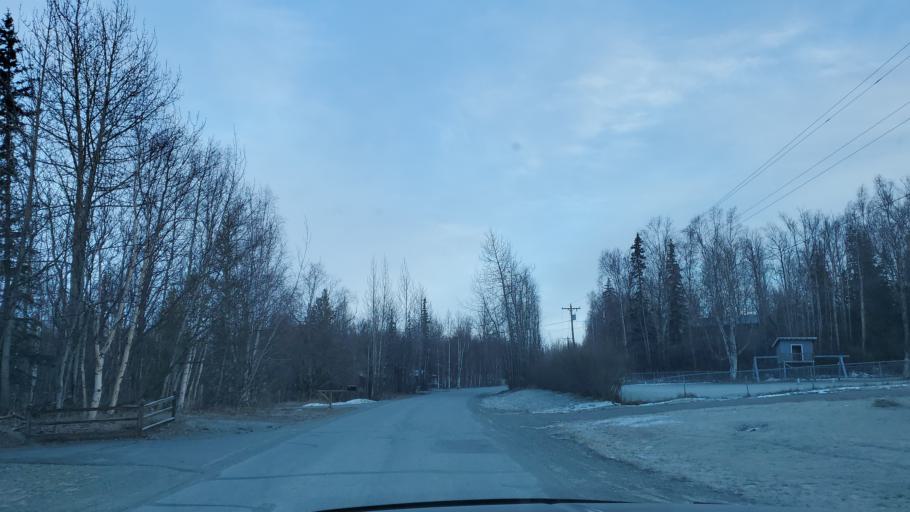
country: US
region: Alaska
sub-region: Matanuska-Susitna Borough
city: Lakes
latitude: 61.6100
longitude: -149.3098
